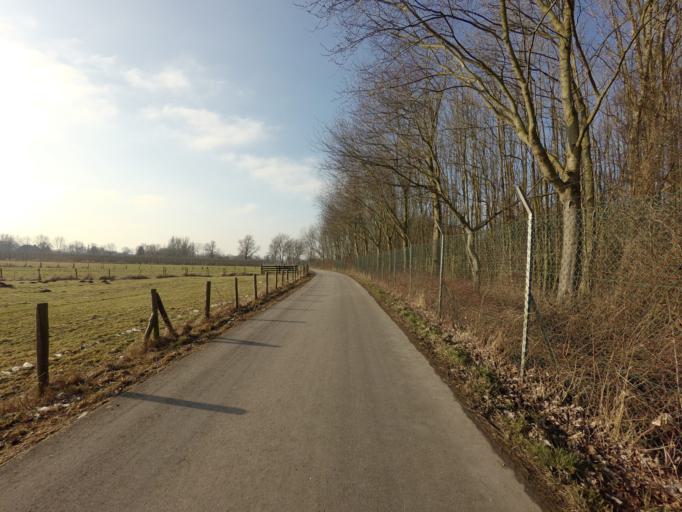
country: NL
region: Utrecht
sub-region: Gemeente Lopik
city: Lopik
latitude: 51.9676
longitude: 4.9591
